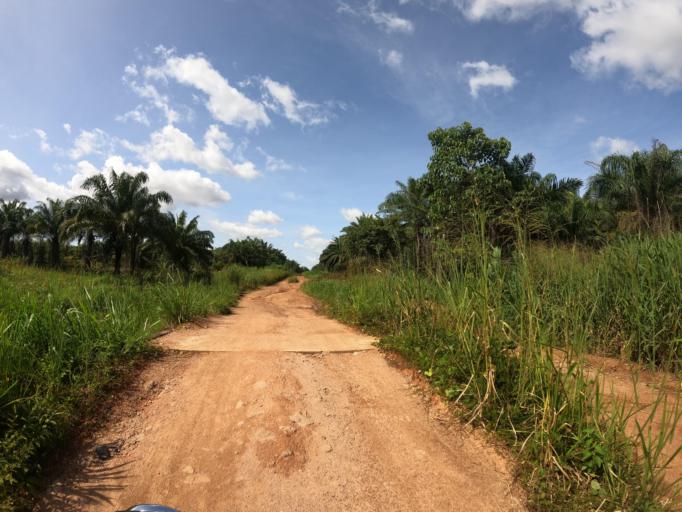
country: SL
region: Northern Province
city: Makeni
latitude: 8.8461
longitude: -12.0303
